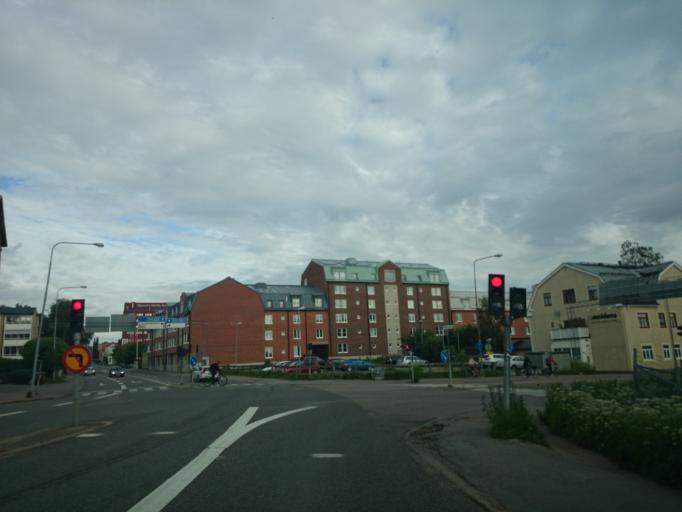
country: SE
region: Vaesternorrland
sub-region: Sundsvalls Kommun
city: Sundsvall
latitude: 62.3853
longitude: 17.3121
